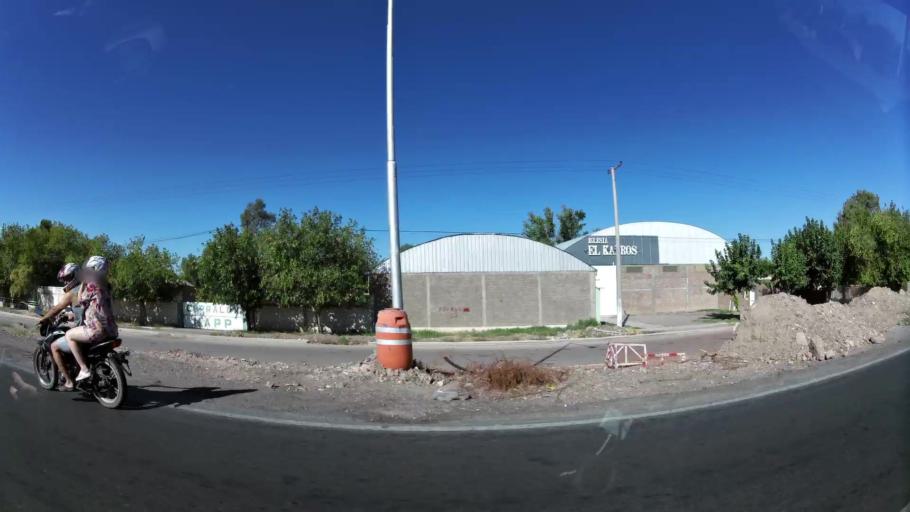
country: AR
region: San Juan
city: Villa Paula de Sarmiento
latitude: -31.5055
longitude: -68.5176
